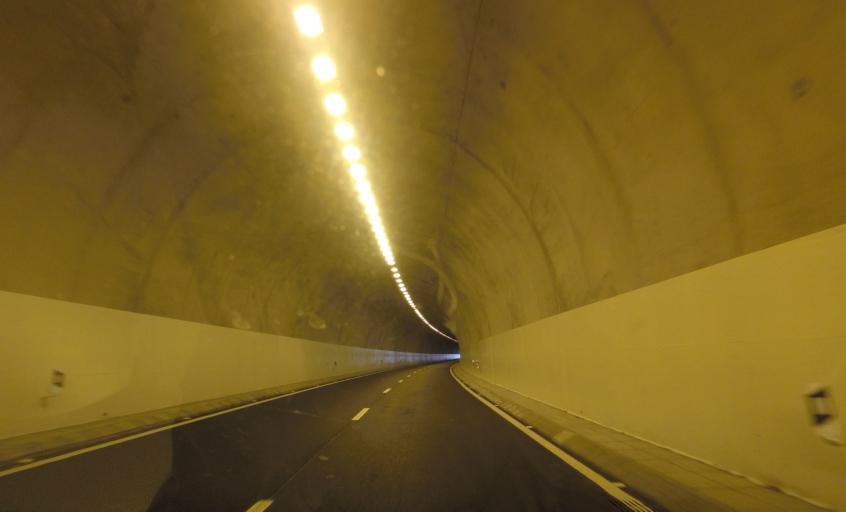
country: PT
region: Madeira
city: Camara de Lobos
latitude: 32.6641
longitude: -16.9691
